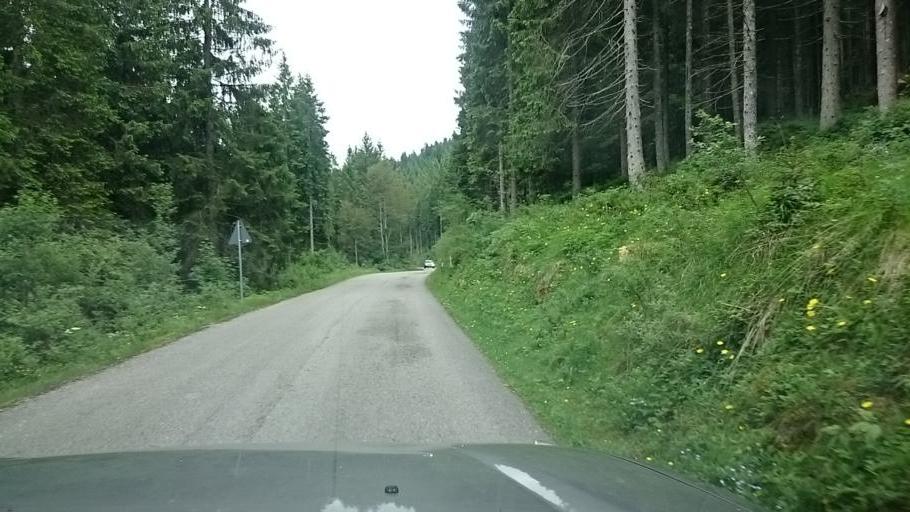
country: IT
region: Veneto
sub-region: Provincia di Vicenza
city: Foza
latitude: 45.9393
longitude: 11.6214
